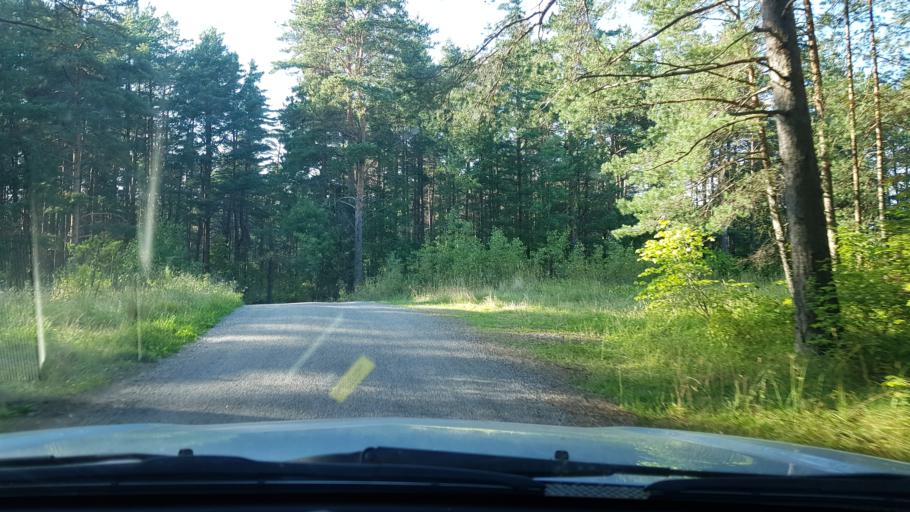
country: EE
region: Ida-Virumaa
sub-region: Narva-Joesuu linn
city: Narva-Joesuu
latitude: 59.4467
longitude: 28.0714
